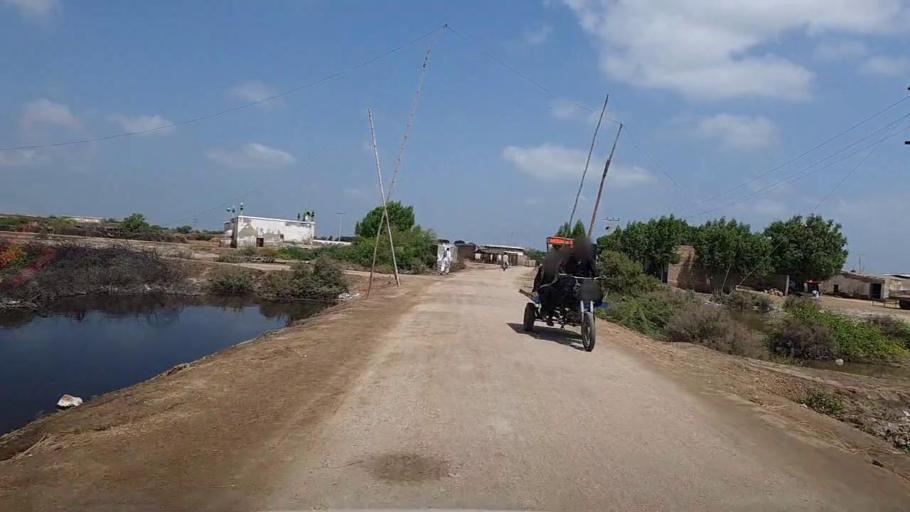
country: PK
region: Sindh
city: Kario
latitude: 24.6773
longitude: 68.5441
